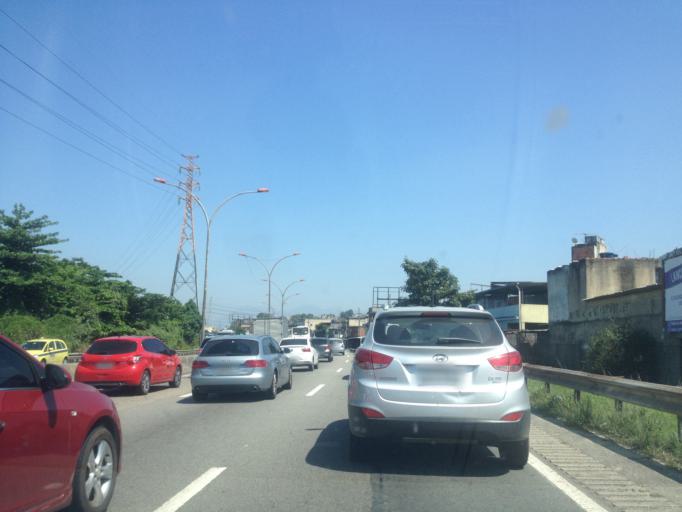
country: BR
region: Rio de Janeiro
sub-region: Duque De Caxias
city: Duque de Caxias
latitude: -22.8004
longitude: -43.3238
